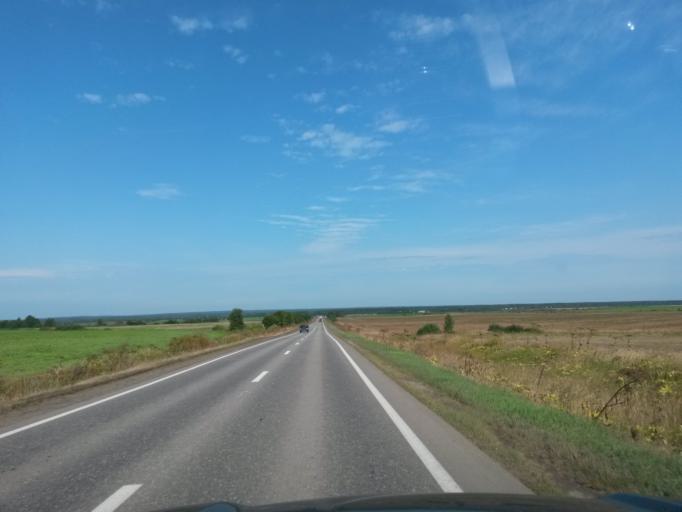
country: RU
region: Jaroslavl
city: Yaroslavl
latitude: 57.7642
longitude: 39.8622
